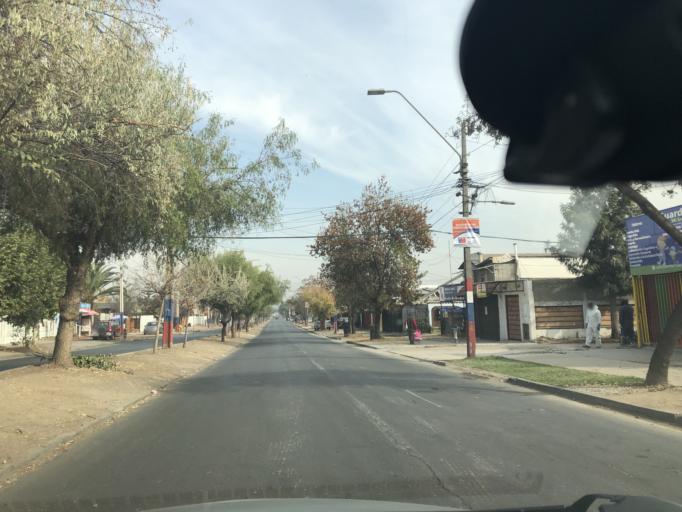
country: CL
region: Santiago Metropolitan
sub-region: Provincia de Cordillera
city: Puente Alto
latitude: -33.5758
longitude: -70.5626
